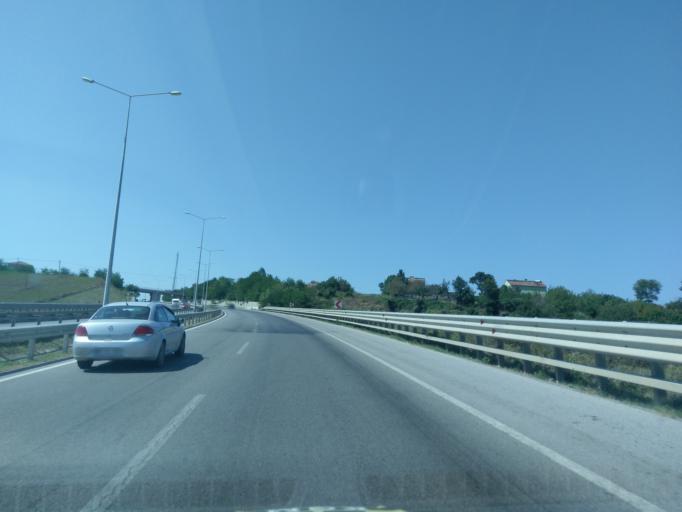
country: TR
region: Samsun
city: Bafra
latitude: 41.5406
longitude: 35.9437
